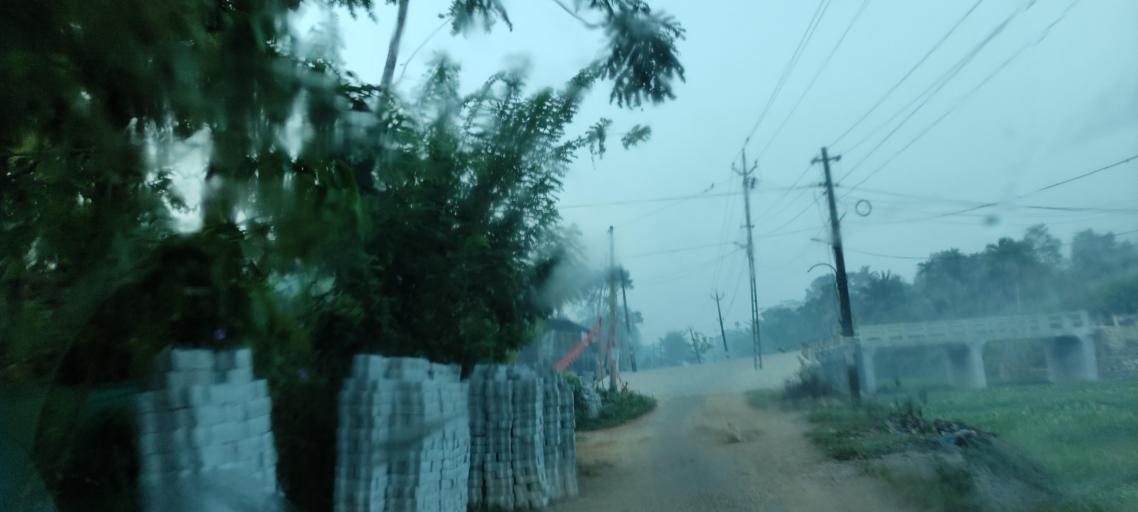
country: IN
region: Kerala
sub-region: Alappuzha
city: Alleppey
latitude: 9.5294
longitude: 76.3293
